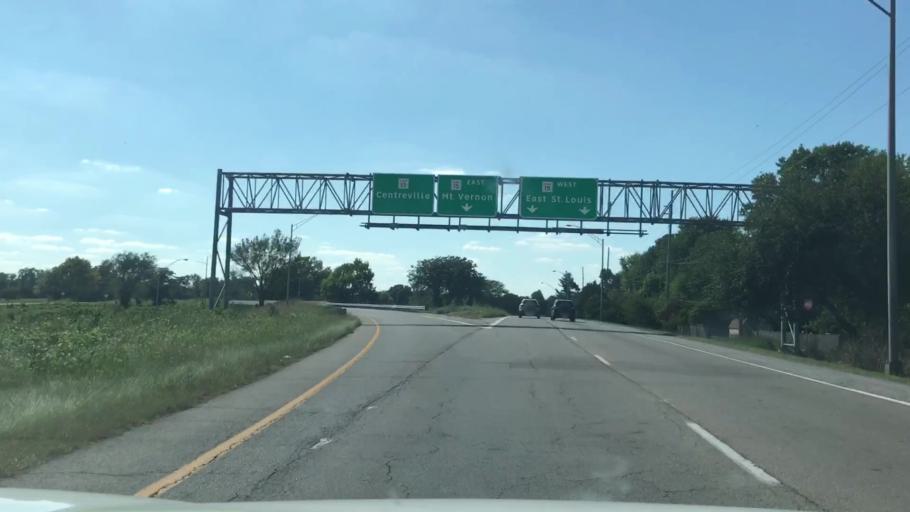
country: US
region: Illinois
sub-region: Saint Clair County
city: Swansea
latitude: 38.5477
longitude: -90.0594
